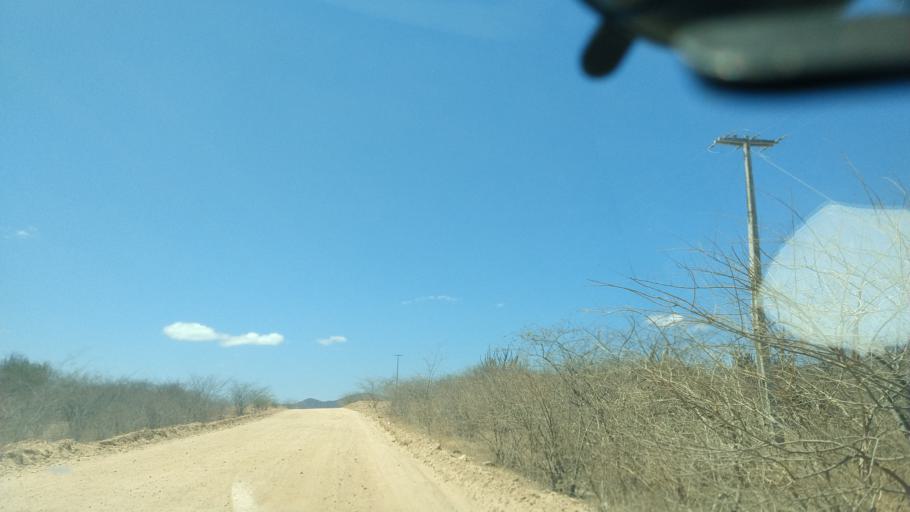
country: BR
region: Rio Grande do Norte
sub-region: Sao Tome
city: Sao Tome
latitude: -5.9750
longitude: -36.1683
